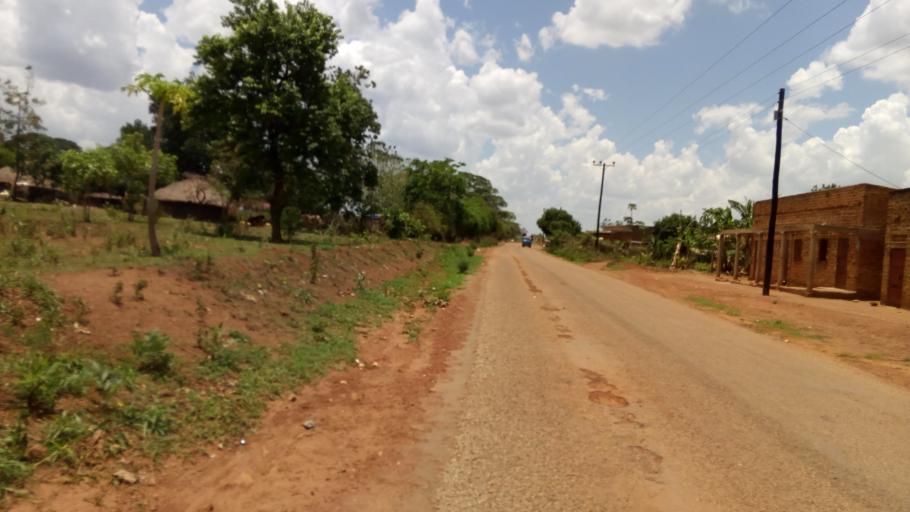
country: UG
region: Northern Region
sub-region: Gulu District
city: Gulu
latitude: 2.7878
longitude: 32.3448
